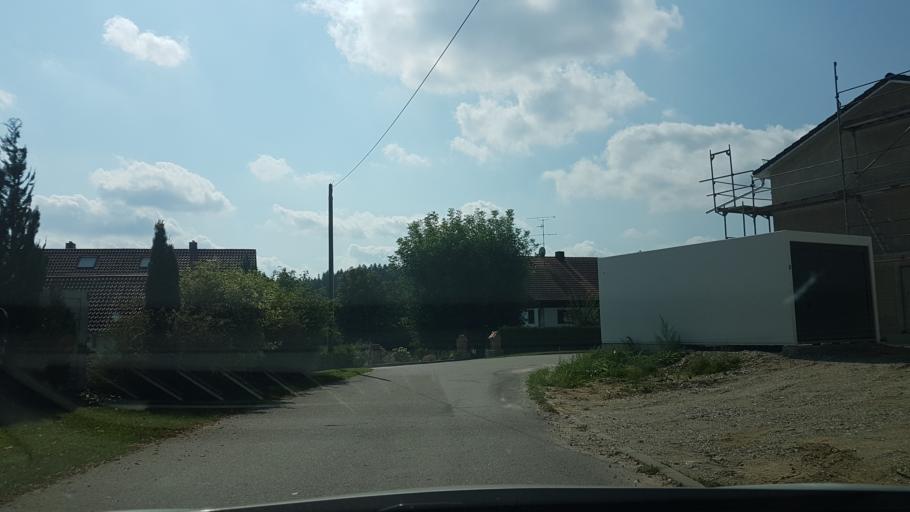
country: DE
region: Bavaria
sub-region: Upper Bavaria
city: Inning am Holz
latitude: 48.3474
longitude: 12.0619
